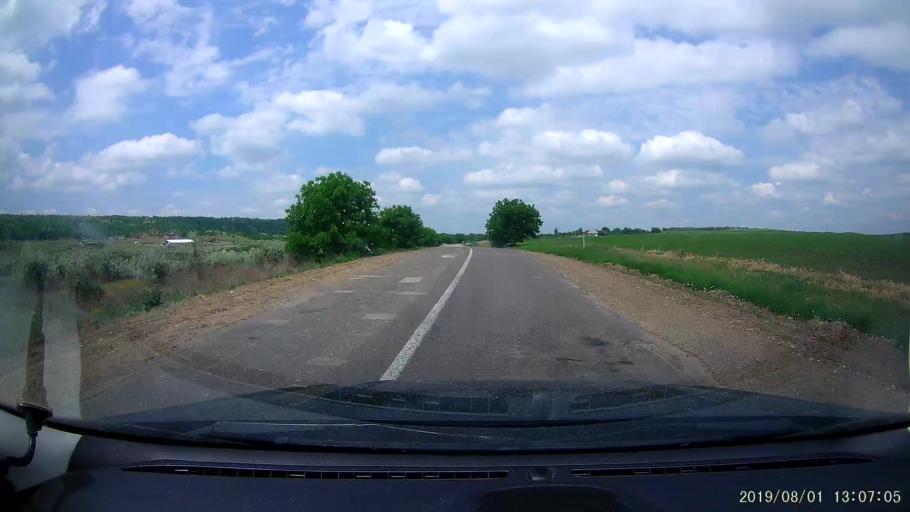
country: MD
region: Gagauzia
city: Vulcanesti
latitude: 45.8067
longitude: 28.3465
